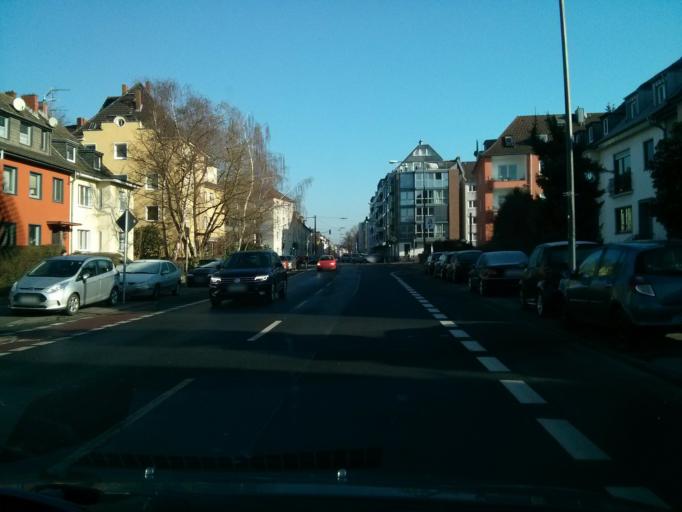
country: DE
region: North Rhine-Westphalia
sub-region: Regierungsbezirk Koln
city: Neustadt/Sued
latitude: 50.9113
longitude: 6.9183
